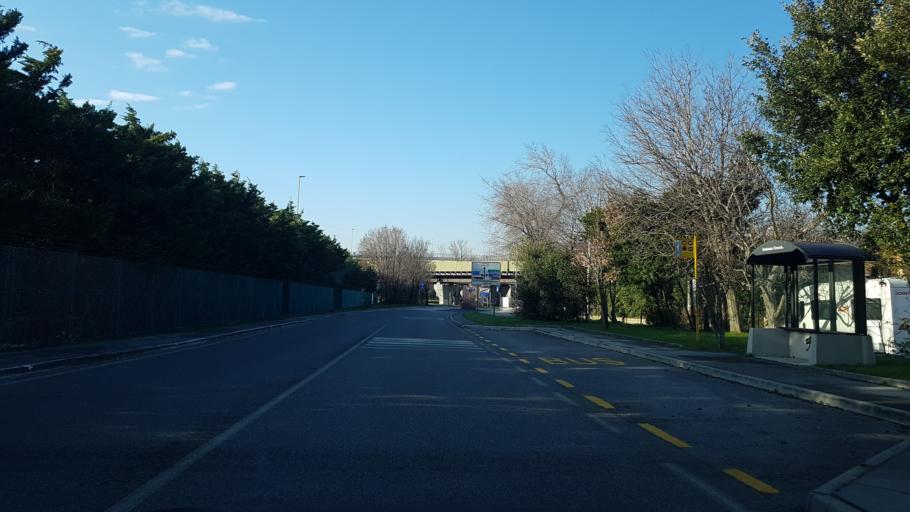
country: IT
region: Friuli Venezia Giulia
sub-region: Provincia di Trieste
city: Domio
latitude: 45.6065
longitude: 13.8338
